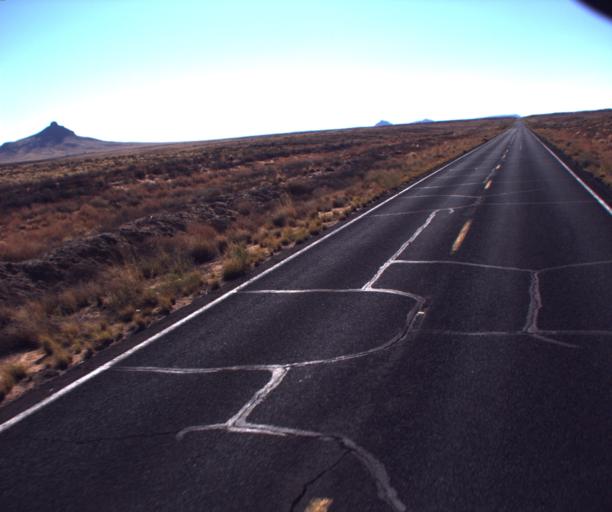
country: US
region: Arizona
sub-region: Navajo County
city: Dilkon
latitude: 35.5678
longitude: -110.4591
